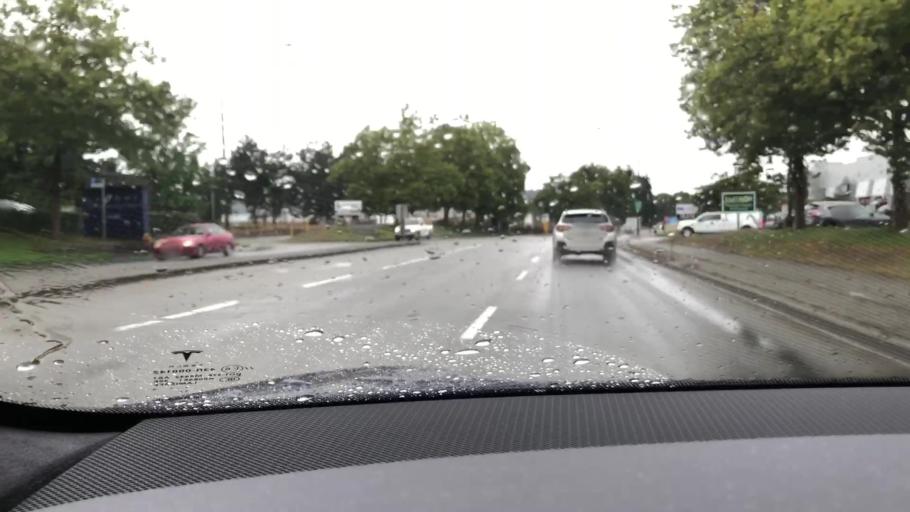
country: CA
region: British Columbia
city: Port Moody
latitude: 49.2296
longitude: -122.8542
